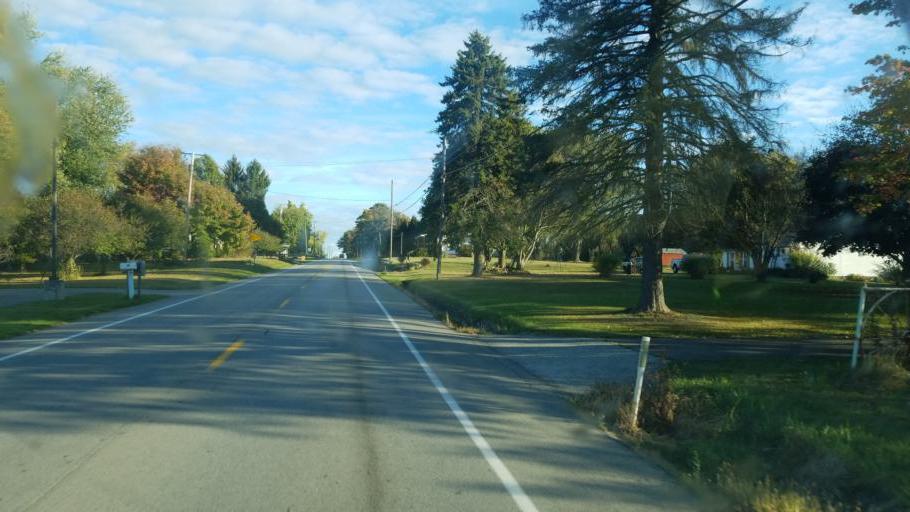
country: US
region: Pennsylvania
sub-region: Mercer County
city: Mercer
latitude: 41.2407
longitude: -80.2382
